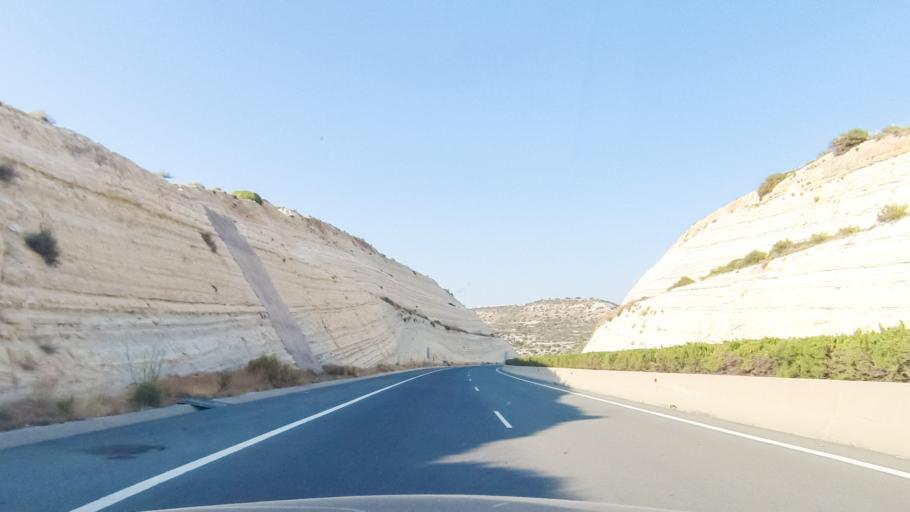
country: CY
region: Limassol
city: Sotira
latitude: 34.6935
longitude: 32.8233
